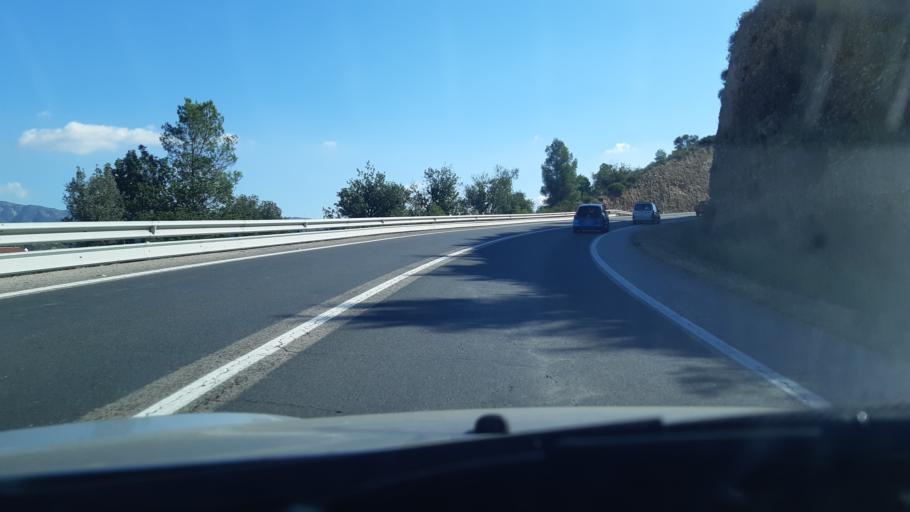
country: ES
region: Catalonia
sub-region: Provincia de Tarragona
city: Tivenys
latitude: 40.8817
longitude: 0.4969
